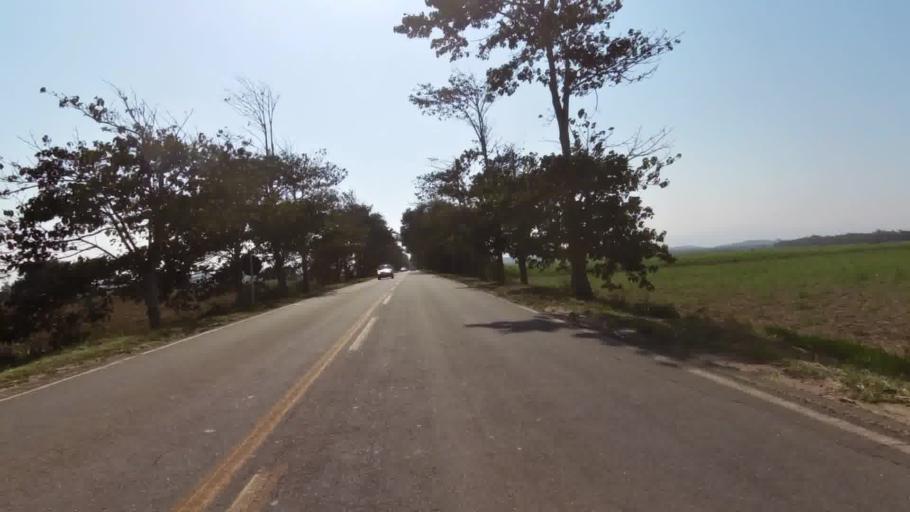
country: BR
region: Espirito Santo
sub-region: Itapemirim
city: Itapemirim
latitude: -20.9995
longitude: -40.8448
